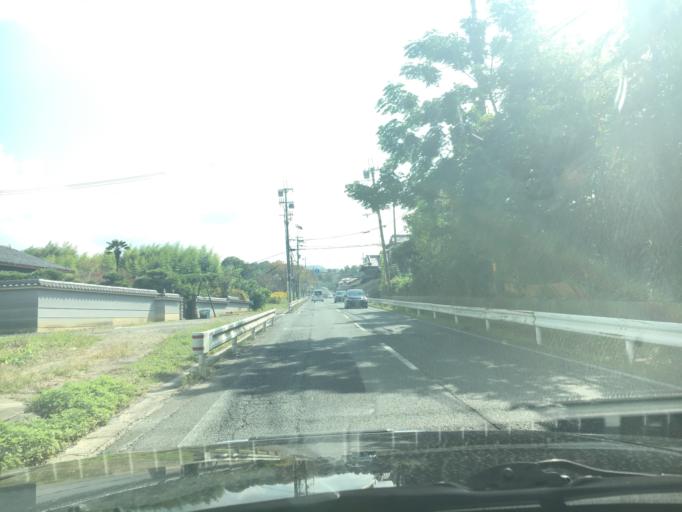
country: JP
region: Nara
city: Nara-shi
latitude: 34.7063
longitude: 135.8329
